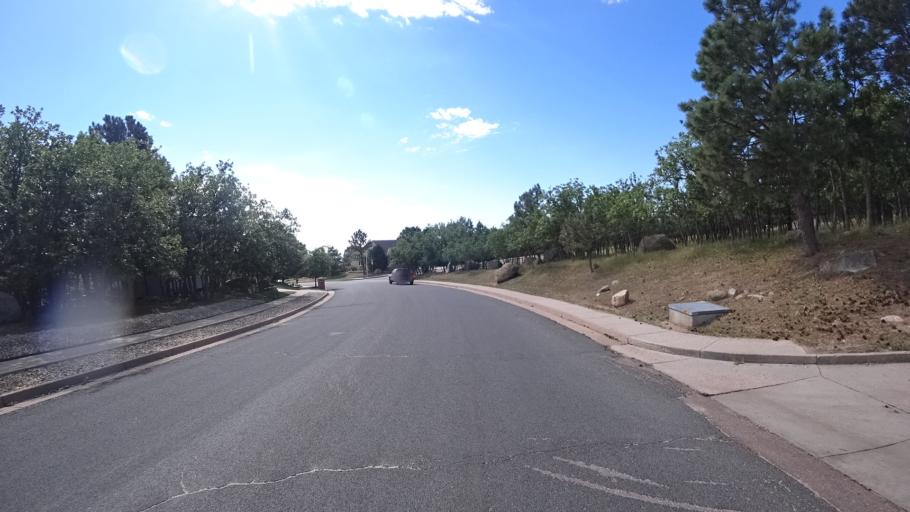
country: US
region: Colorado
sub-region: El Paso County
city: Fort Carson
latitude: 38.7607
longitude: -104.8322
